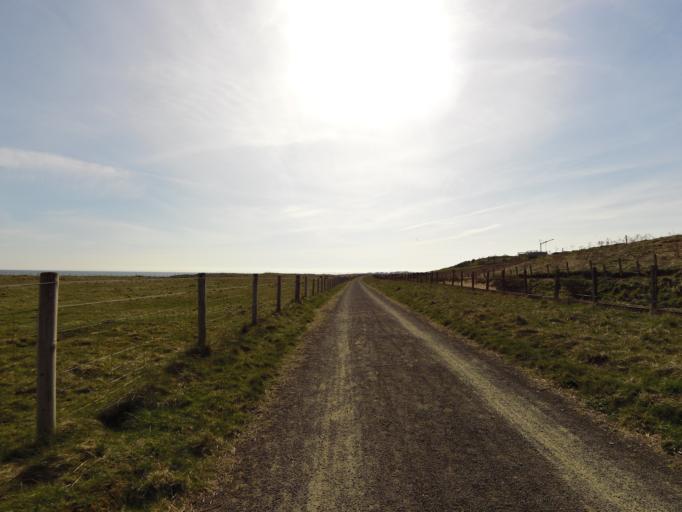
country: GB
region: Scotland
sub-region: Angus
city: Arbroath
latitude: 56.5265
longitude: -2.6411
